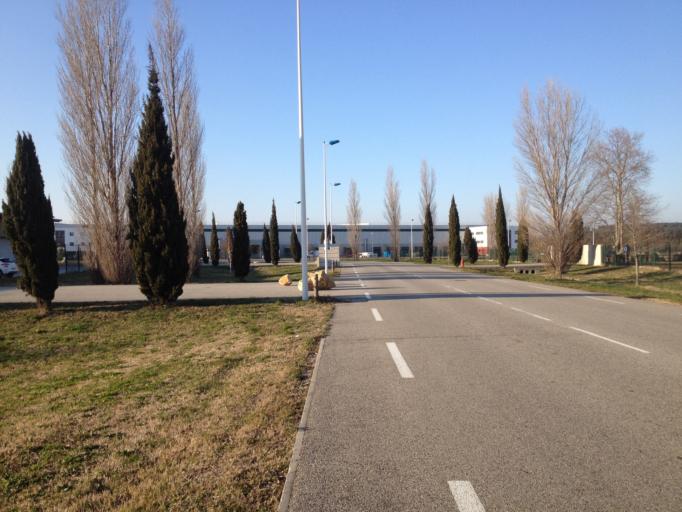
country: FR
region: Provence-Alpes-Cote d'Azur
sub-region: Departement du Vaucluse
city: Vedene
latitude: 43.9897
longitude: 4.8960
